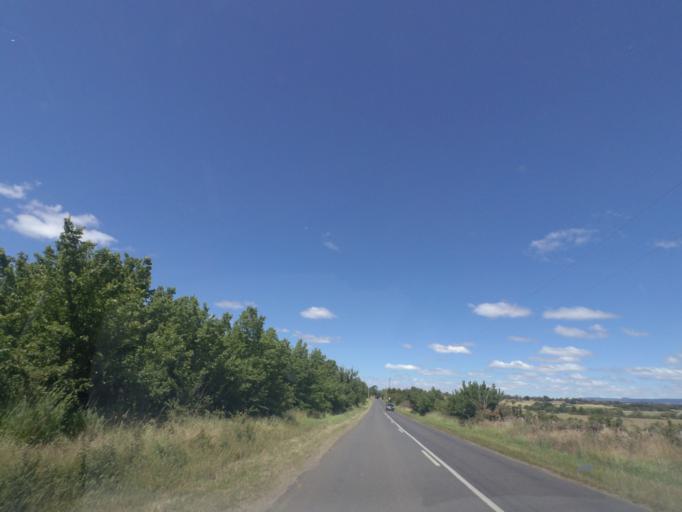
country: AU
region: Victoria
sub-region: Mount Alexander
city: Castlemaine
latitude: -37.2372
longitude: 144.4093
